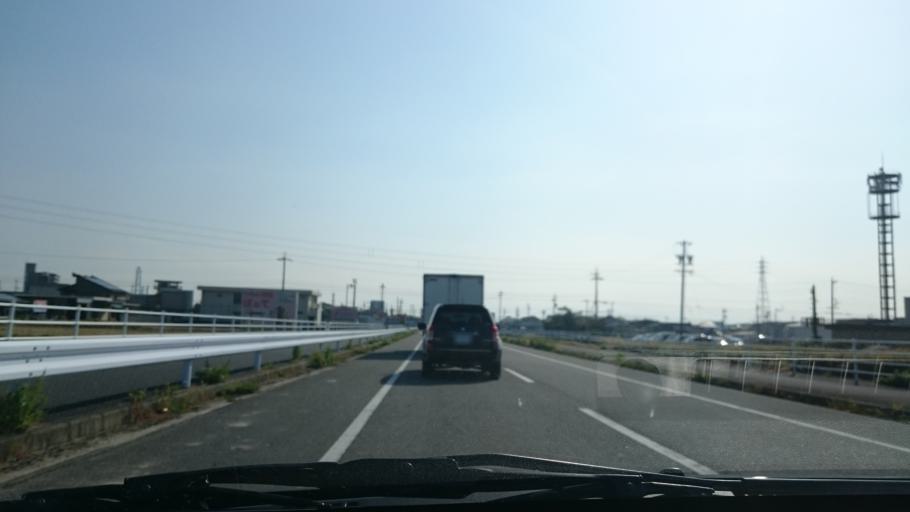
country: JP
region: Mie
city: Yokkaichi
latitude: 34.9844
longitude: 136.6179
